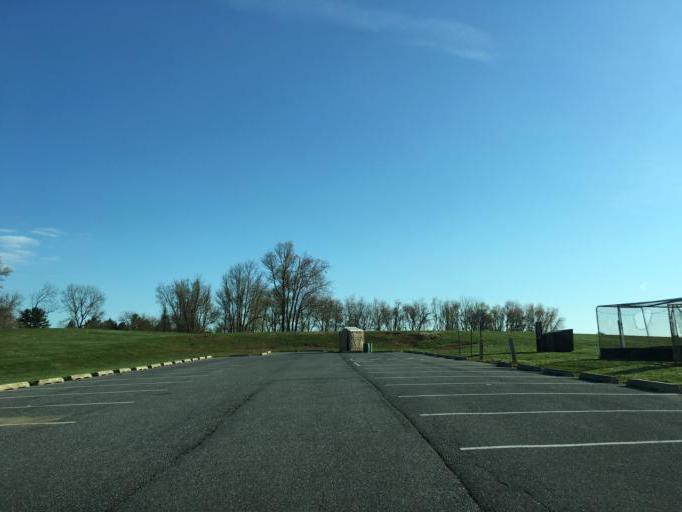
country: US
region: Maryland
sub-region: Baltimore County
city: Timonium
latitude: 39.4703
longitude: -76.6037
